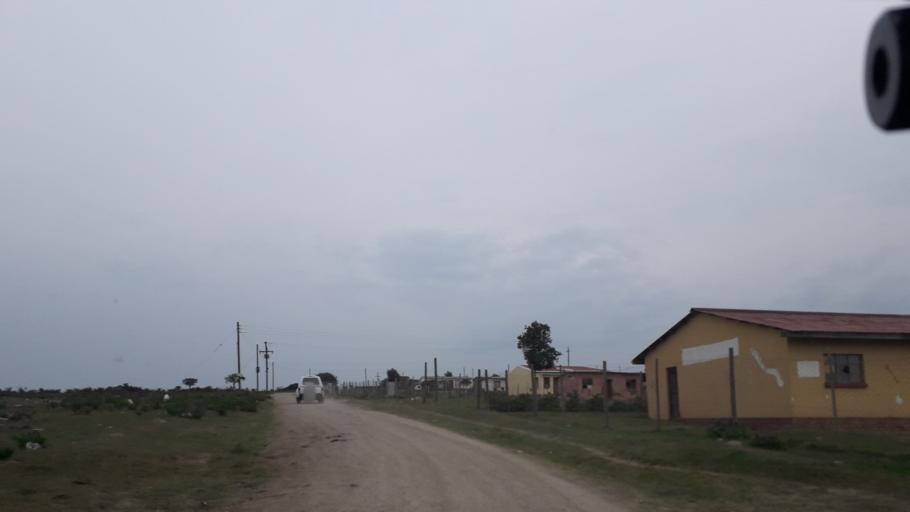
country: ZA
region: Eastern Cape
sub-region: Buffalo City Metropolitan Municipality
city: Bhisho
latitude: -32.8339
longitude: 27.3726
